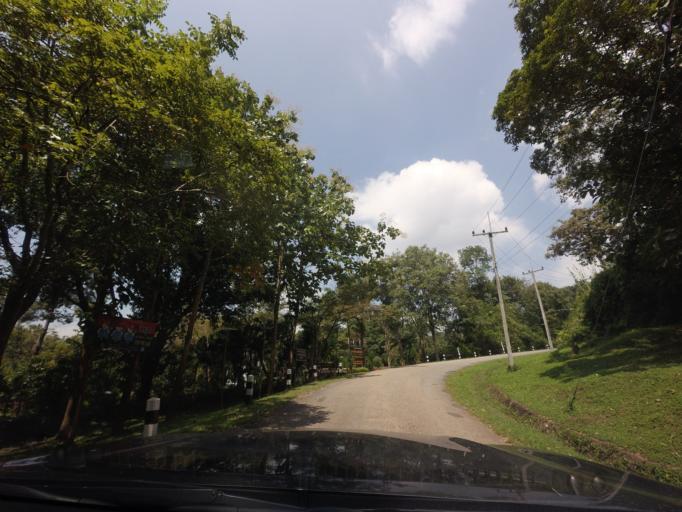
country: TH
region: Loei
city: Phu Ruea
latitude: 17.4649
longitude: 101.3547
